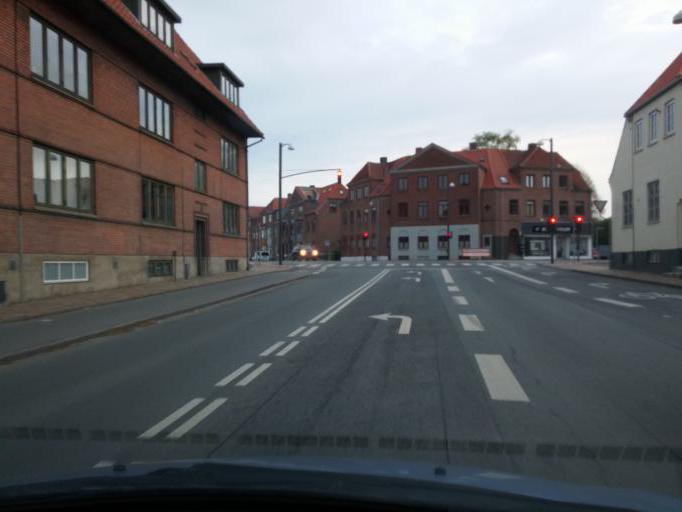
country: DK
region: South Denmark
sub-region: Odense Kommune
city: Odense
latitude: 55.4032
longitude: 10.4002
